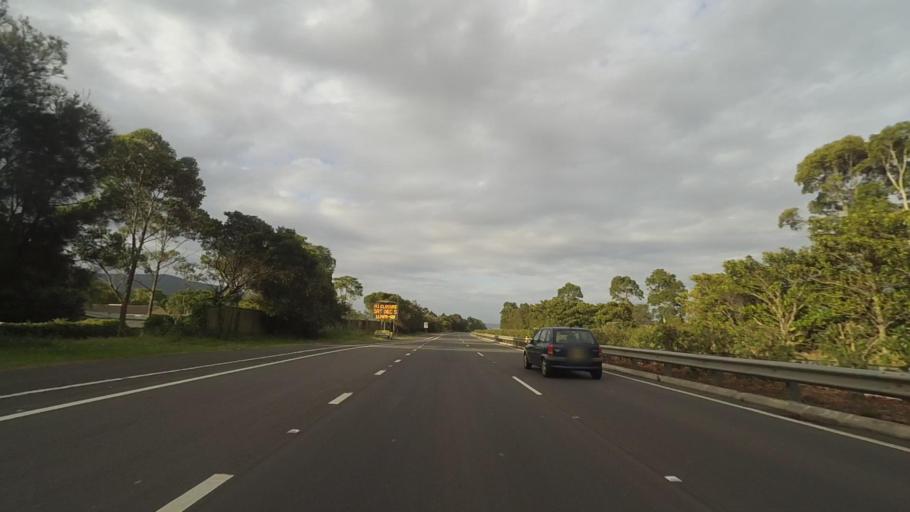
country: AU
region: New South Wales
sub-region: Wollongong
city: Fairy Meadow
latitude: -34.4018
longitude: 150.8931
